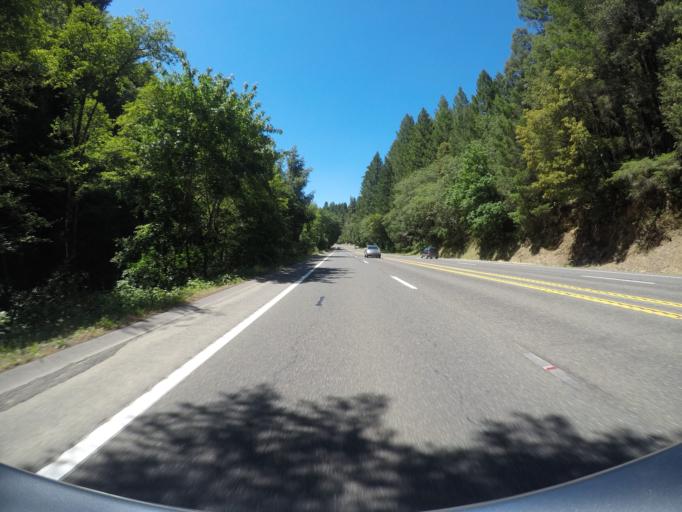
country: US
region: California
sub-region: Mendocino County
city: Laytonville
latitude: 39.5758
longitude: -123.4392
